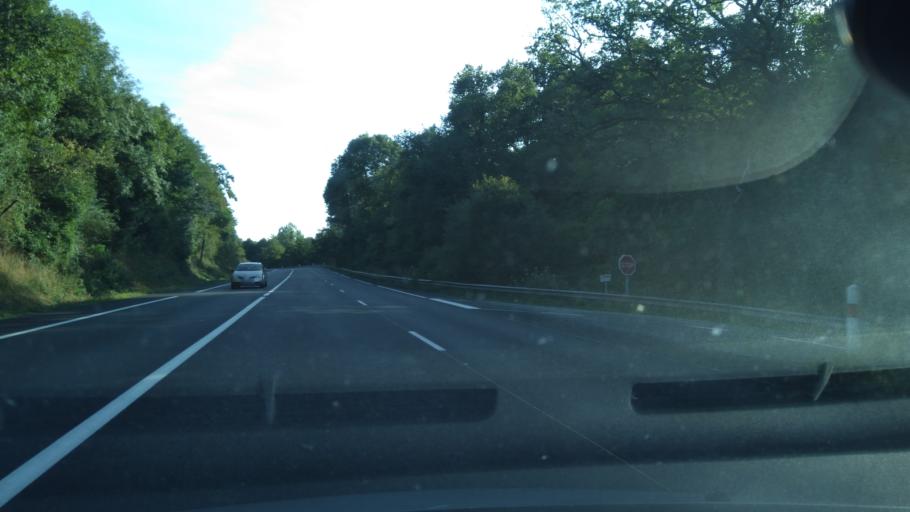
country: FR
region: Pays de la Loire
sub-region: Departement de la Mayenne
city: Entrammes
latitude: 47.9695
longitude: -0.7073
